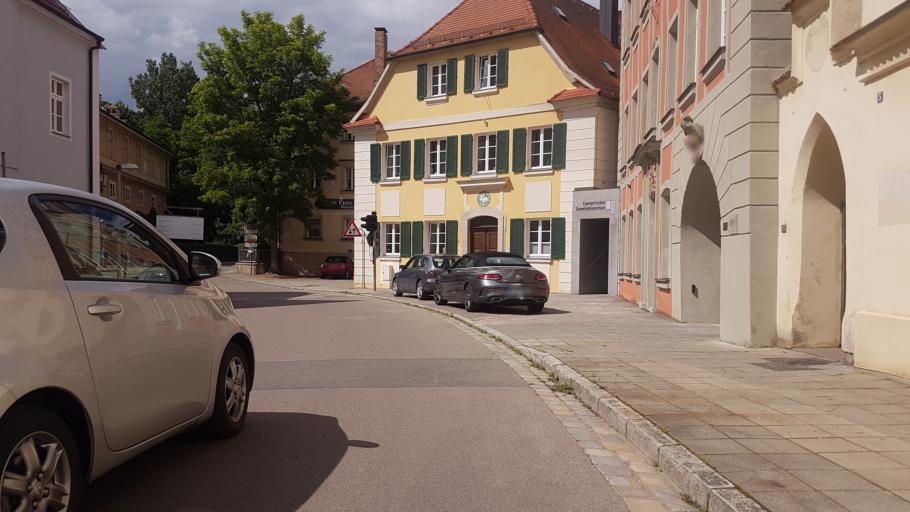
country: DE
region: Bavaria
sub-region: Regierungsbezirk Mittelfranken
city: Pappenheim
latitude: 48.9343
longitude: 10.9749
